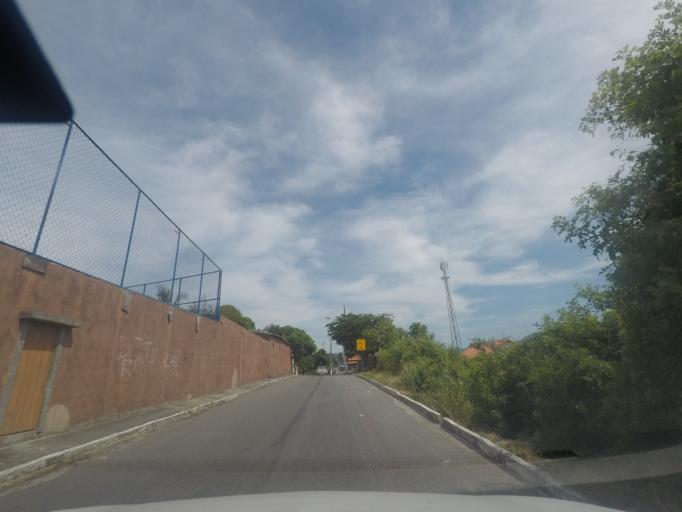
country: BR
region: Rio de Janeiro
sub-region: Marica
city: Marica
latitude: -22.9541
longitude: -42.7491
